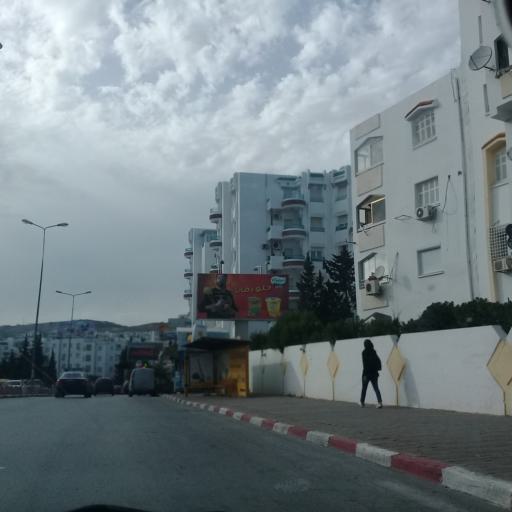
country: TN
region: Ariana
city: Ariana
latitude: 36.8581
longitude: 10.1664
